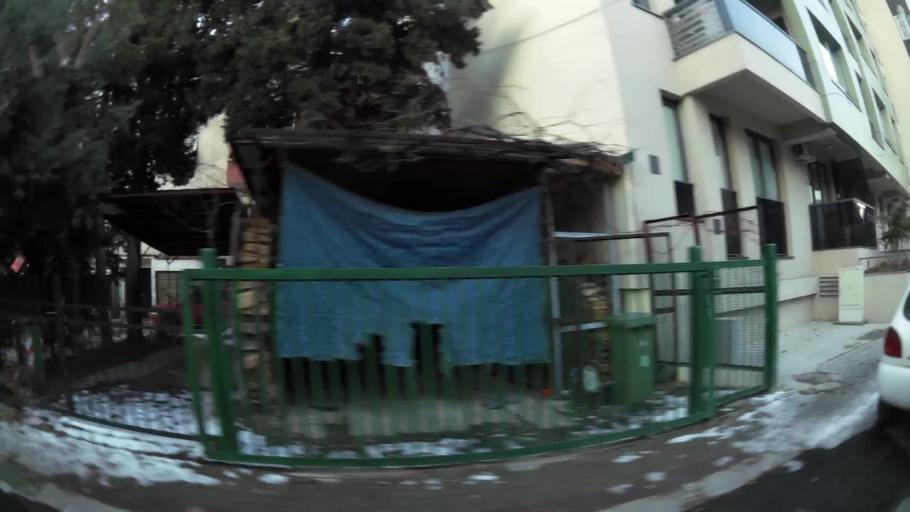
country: MK
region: Karpos
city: Skopje
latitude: 41.9912
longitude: 21.4187
